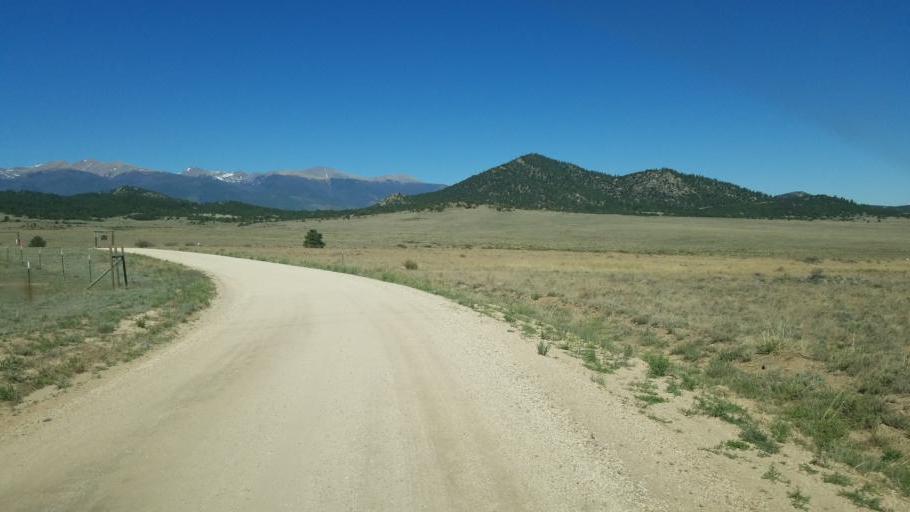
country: US
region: Colorado
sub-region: Custer County
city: Westcliffe
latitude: 38.2344
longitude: -105.5001
